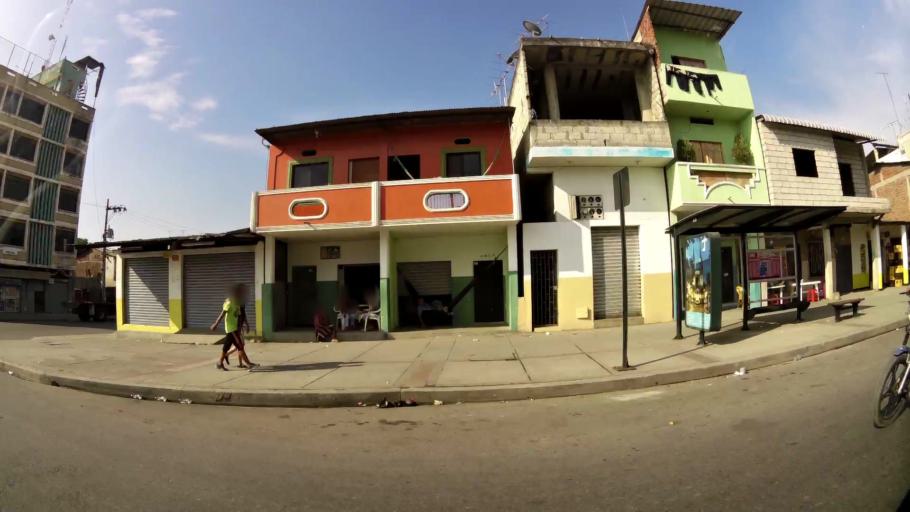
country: EC
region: Guayas
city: Santa Lucia
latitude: -2.0685
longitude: -79.9346
